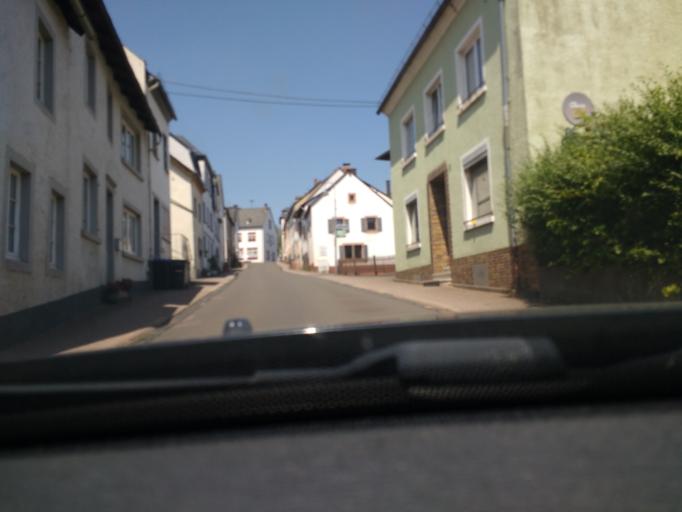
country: DE
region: Rheinland-Pfalz
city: Manderscheid
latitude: 50.0920
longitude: 6.8132
